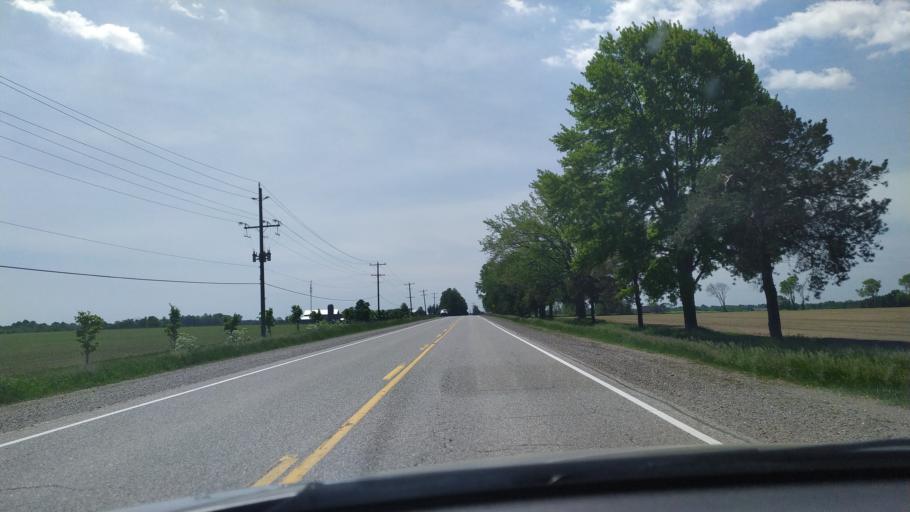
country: CA
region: Ontario
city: Dorchester
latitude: 43.0840
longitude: -81.0020
